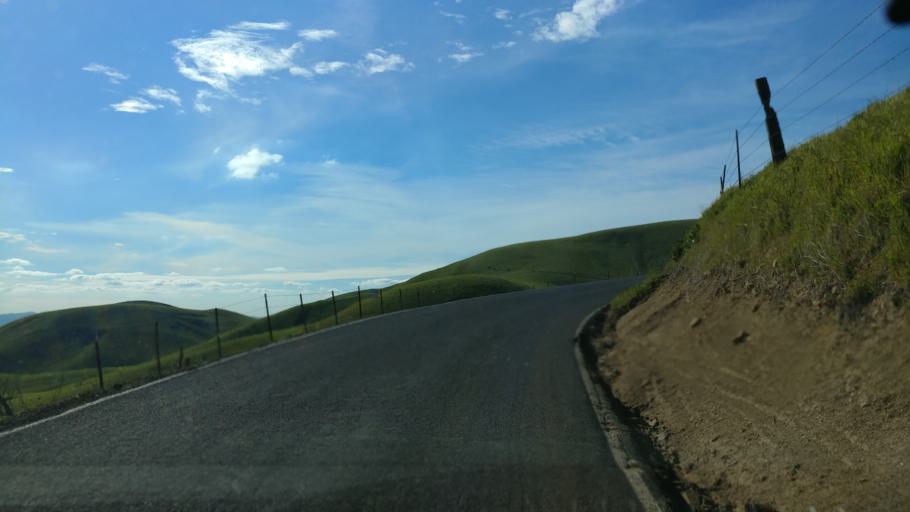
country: US
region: California
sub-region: Alameda County
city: Livermore
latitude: 37.7890
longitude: -121.7725
